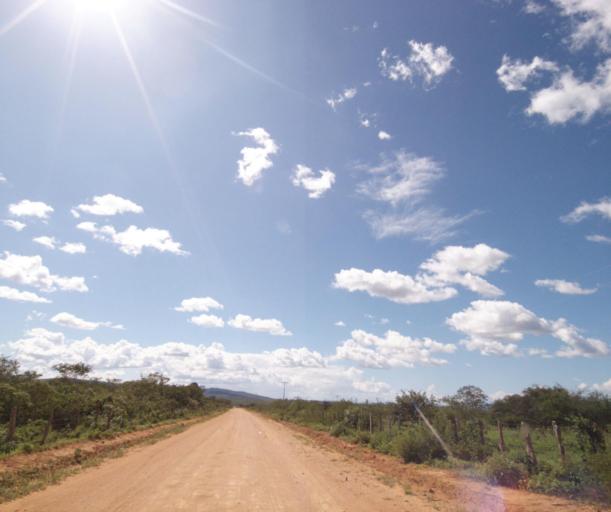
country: BR
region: Bahia
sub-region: Pocoes
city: Pocoes
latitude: -14.2475
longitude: -40.7518
